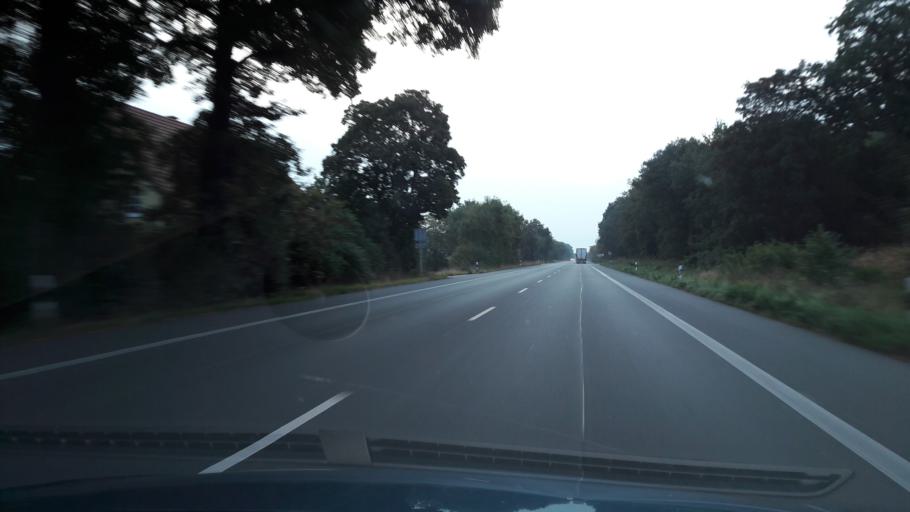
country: DE
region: North Rhine-Westphalia
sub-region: Regierungsbezirk Munster
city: Telgte
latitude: 51.9281
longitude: 7.7675
